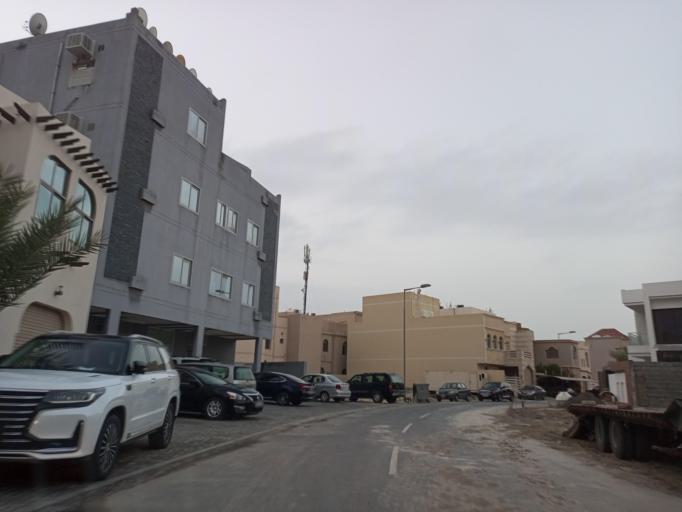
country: BH
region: Muharraq
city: Al Hadd
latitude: 26.2314
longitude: 50.6528
